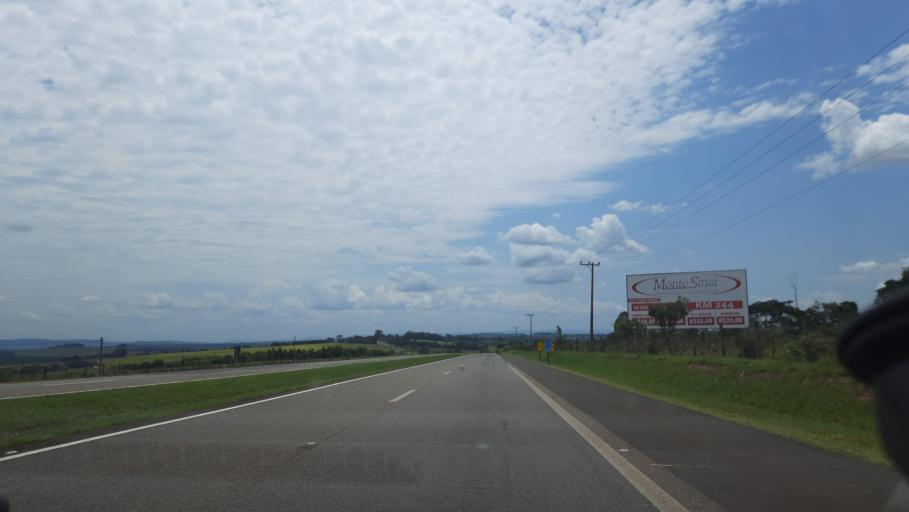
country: BR
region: Sao Paulo
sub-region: Casa Branca
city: Casa Branca
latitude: -21.7412
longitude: -47.0729
